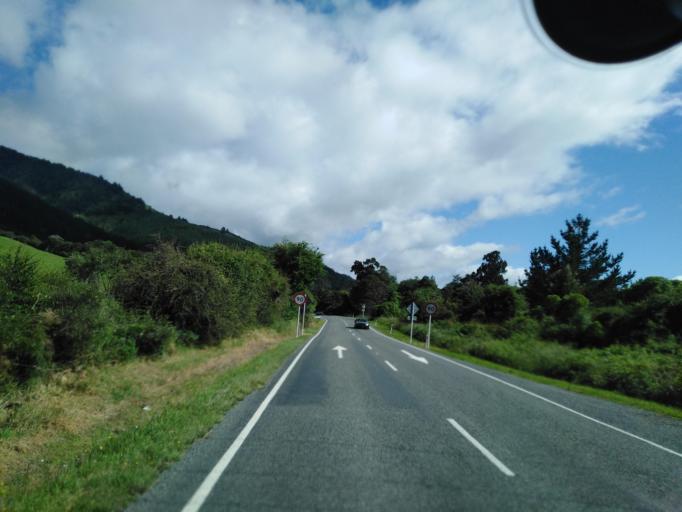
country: NZ
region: Nelson
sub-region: Nelson City
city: Nelson
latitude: -41.2931
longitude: 173.5735
